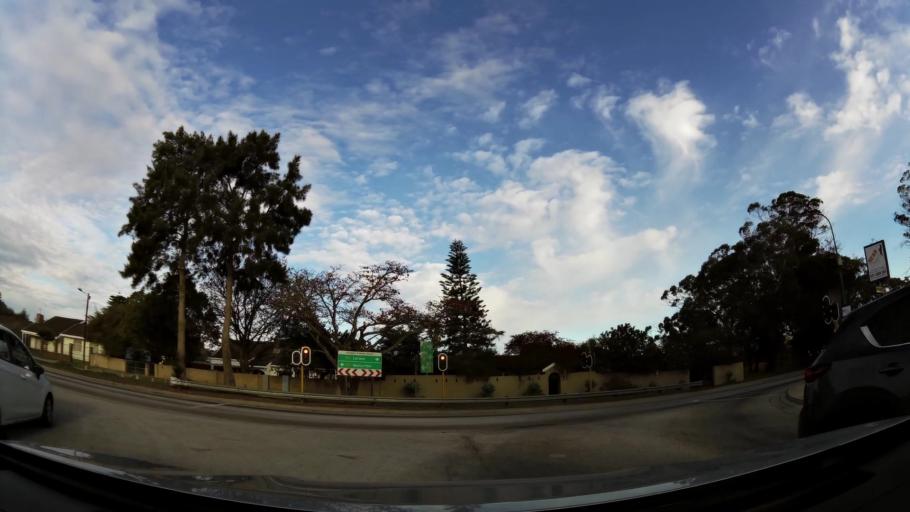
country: ZA
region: Eastern Cape
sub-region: Nelson Mandela Bay Metropolitan Municipality
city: Port Elizabeth
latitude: -33.9549
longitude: 25.5199
